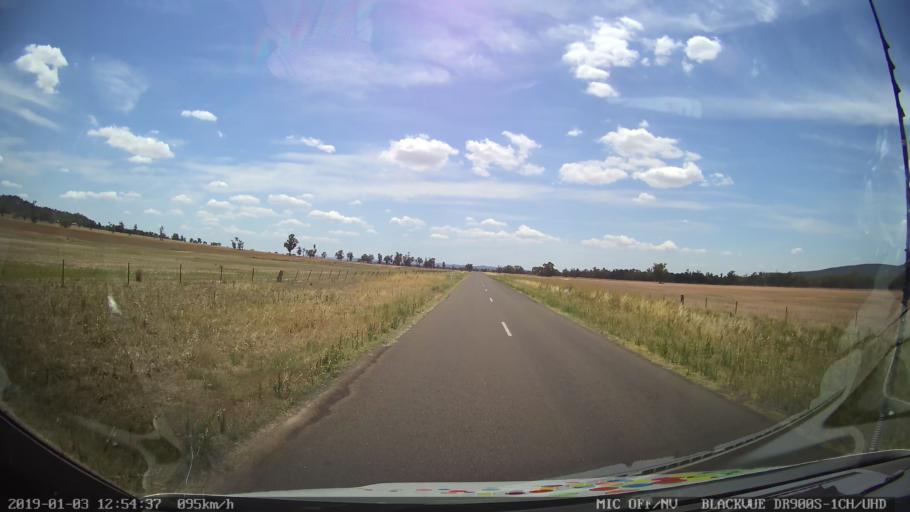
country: AU
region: New South Wales
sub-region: Weddin
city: Grenfell
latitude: -33.6509
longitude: 148.3193
